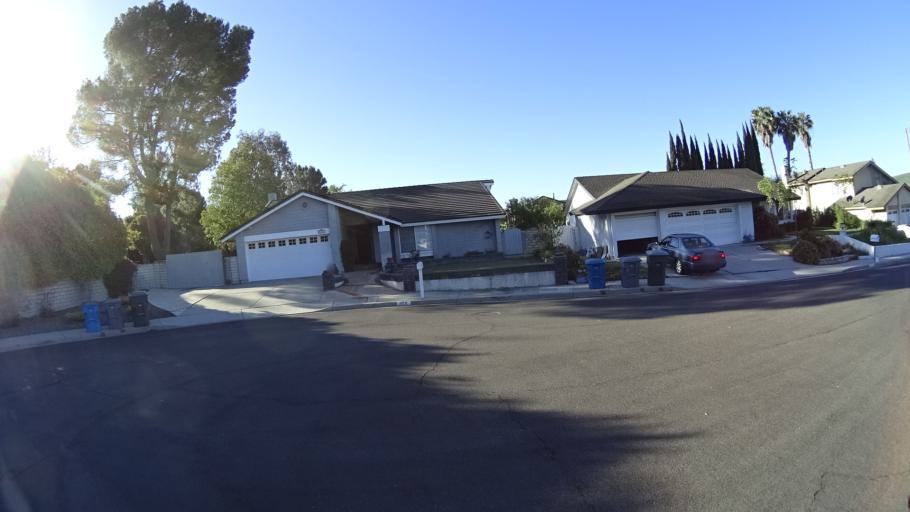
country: US
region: California
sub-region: Ventura County
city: Casa Conejo
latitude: 34.2184
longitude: -118.8898
